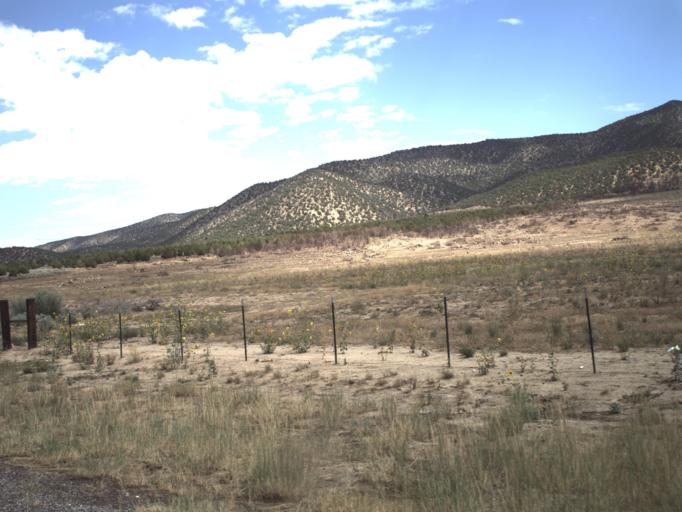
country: US
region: Utah
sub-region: Sanpete County
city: Gunnison
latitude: 39.1887
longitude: -112.0787
